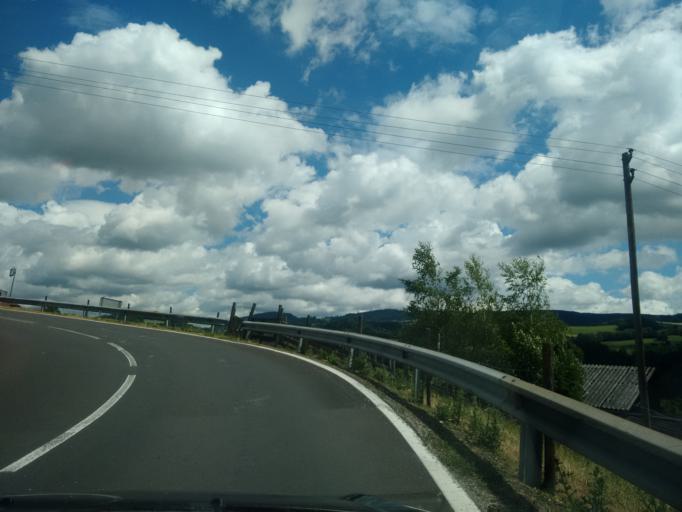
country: AT
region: Upper Austria
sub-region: Politischer Bezirk Urfahr-Umgebung
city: Gramastetten
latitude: 48.3861
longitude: 14.1930
